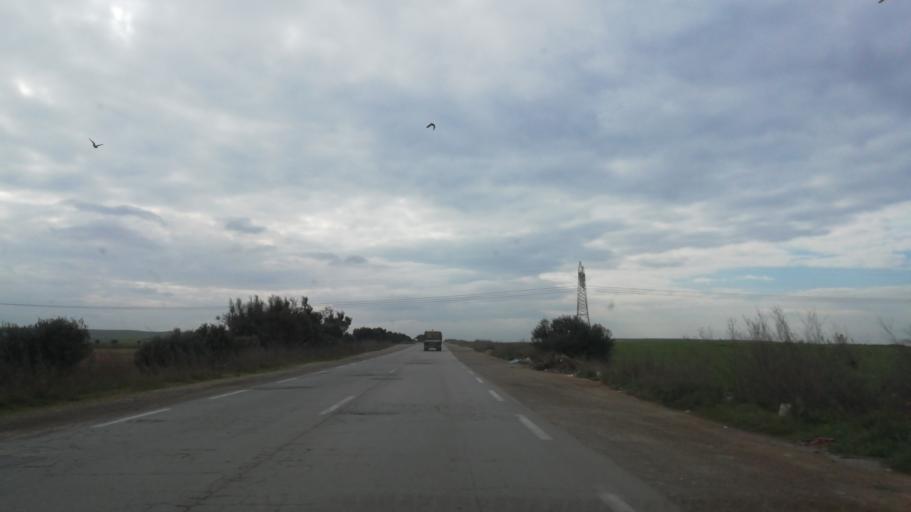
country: DZ
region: Oran
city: Ain el Bya
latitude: 35.7684
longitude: -0.3479
